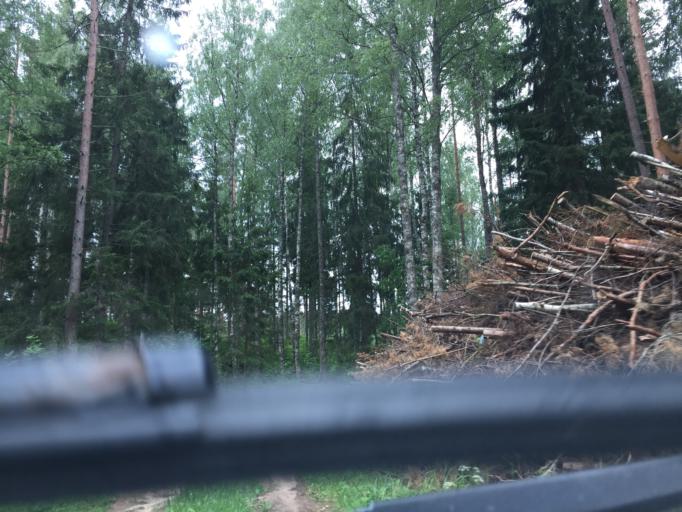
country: LV
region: Tukuma Rajons
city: Tukums
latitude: 57.0312
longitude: 23.0759
